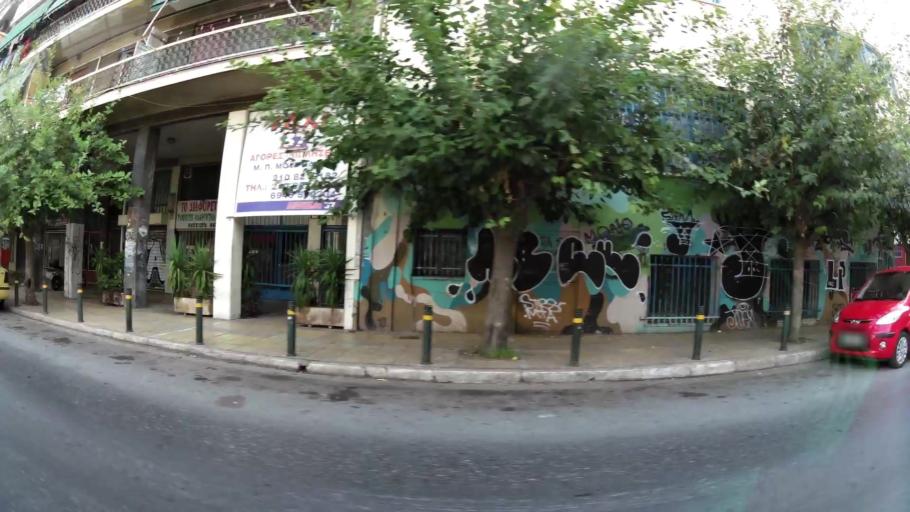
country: GR
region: Attica
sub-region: Nomarchia Athinas
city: Athens
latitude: 37.9903
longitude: 23.7241
